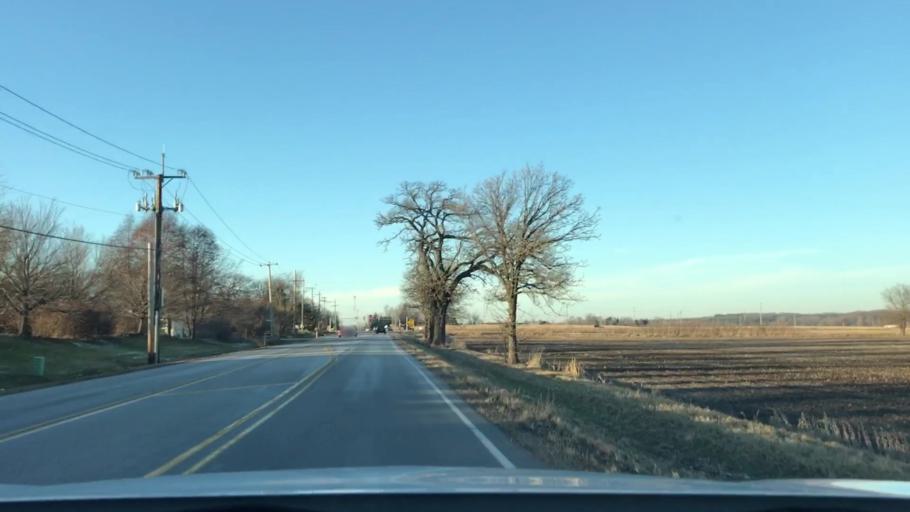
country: US
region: Illinois
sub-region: Kane County
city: Pingree Grove
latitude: 42.0943
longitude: -88.4002
